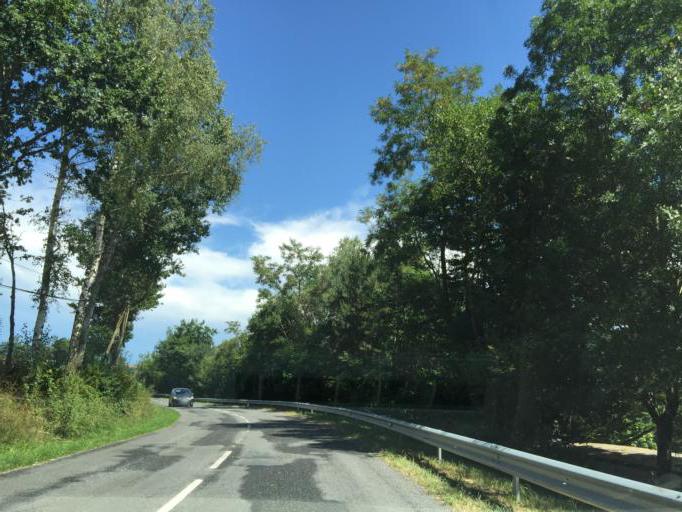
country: FR
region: Midi-Pyrenees
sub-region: Departement de l'Aveyron
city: Pont-de-Salars
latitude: 44.3031
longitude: 2.7329
